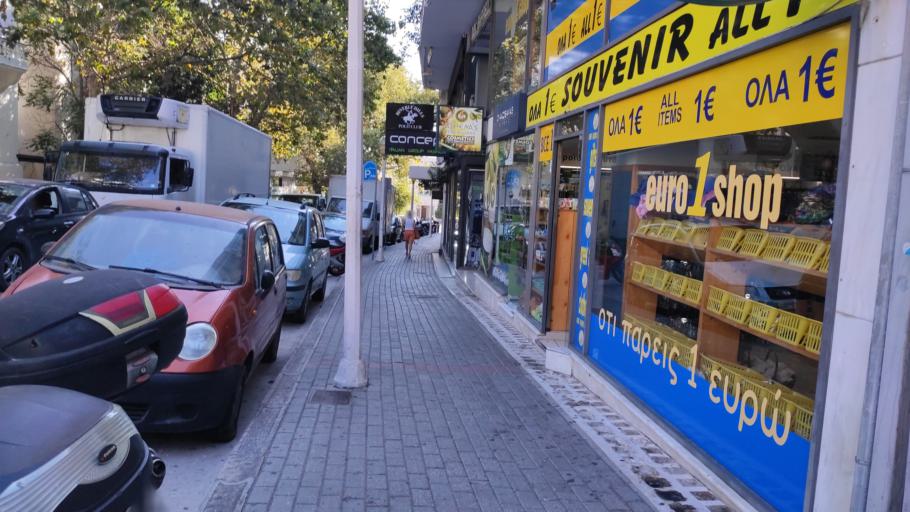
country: GR
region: South Aegean
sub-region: Nomos Dodekanisou
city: Rodos
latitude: 36.4479
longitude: 28.2228
